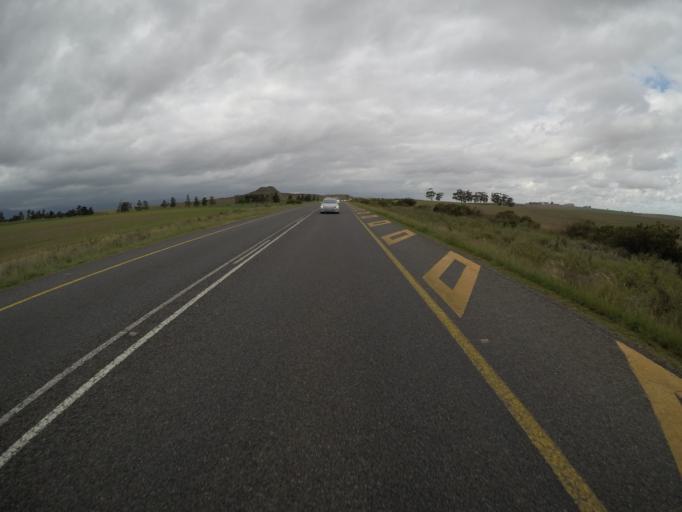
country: ZA
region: Western Cape
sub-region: Overberg District Municipality
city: Swellendam
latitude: -34.1028
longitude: 20.7915
